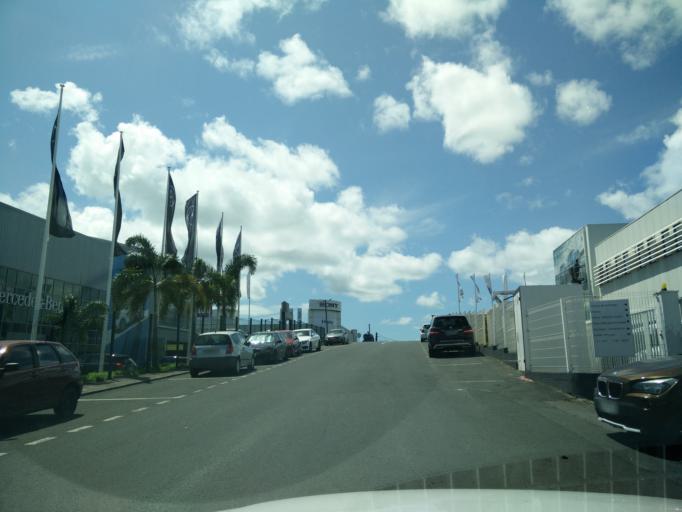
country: GP
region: Guadeloupe
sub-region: Guadeloupe
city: Pointe-a-Pitre
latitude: 16.2414
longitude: -61.5629
